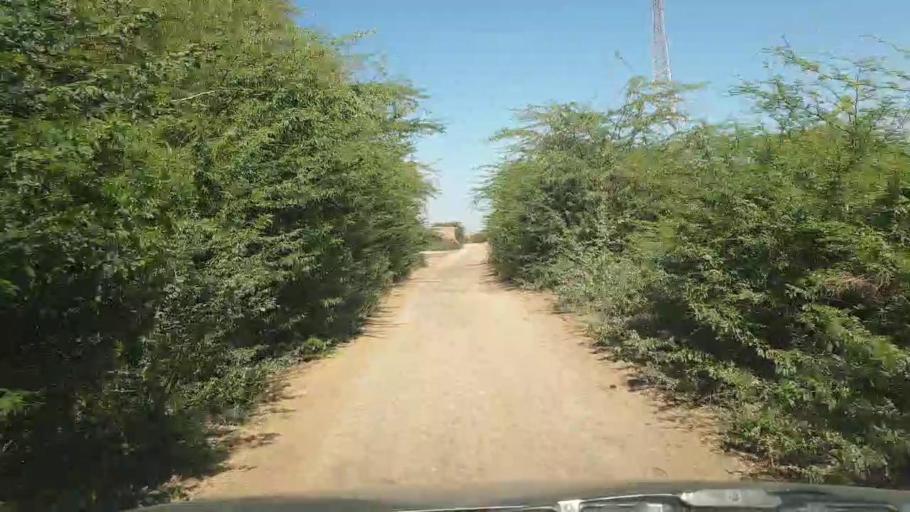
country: PK
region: Sindh
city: Umarkot
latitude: 25.4062
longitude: 69.6363
